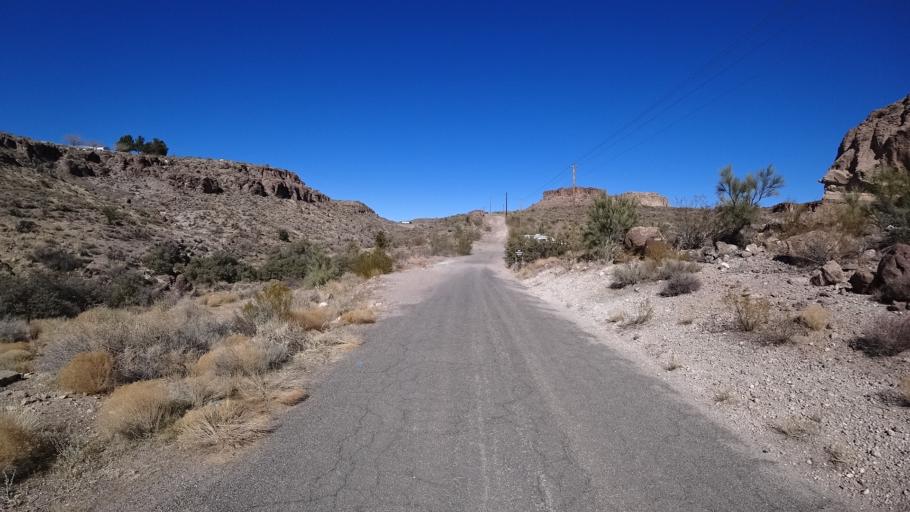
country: US
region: Arizona
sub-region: Mohave County
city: Kingman
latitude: 35.2014
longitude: -114.0571
